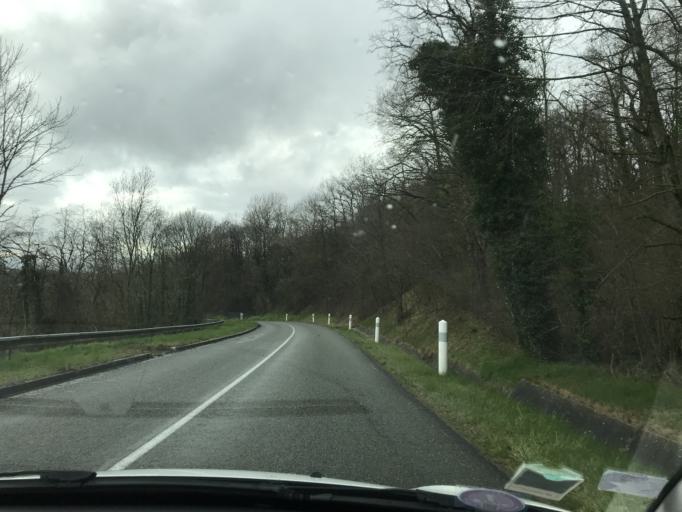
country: FR
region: Picardie
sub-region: Departement de l'Aisne
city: Belleu
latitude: 49.3595
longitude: 3.3489
